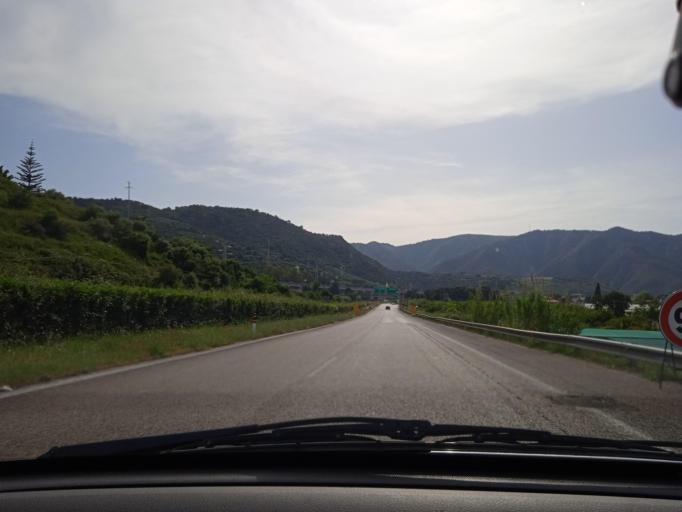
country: IT
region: Sicily
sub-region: Messina
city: Falcone
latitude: 38.1139
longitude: 15.0801
